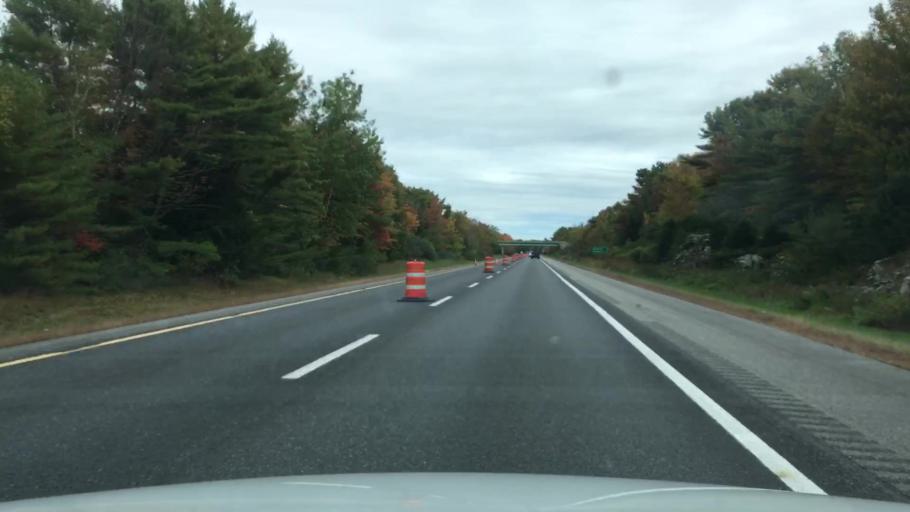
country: US
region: Maine
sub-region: Sagadahoc County
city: Richmond
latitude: 44.1103
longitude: -69.8603
